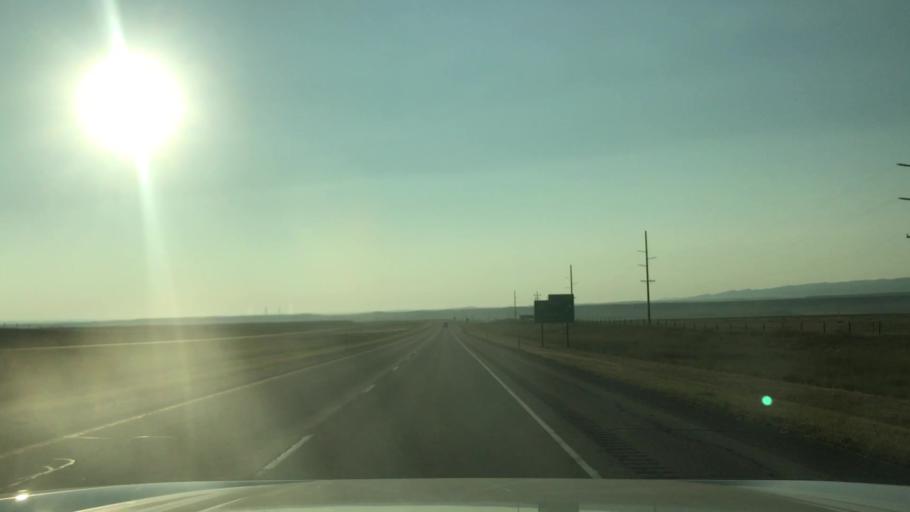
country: US
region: Wyoming
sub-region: Converse County
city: Glenrock
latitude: 42.8382
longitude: -105.9062
